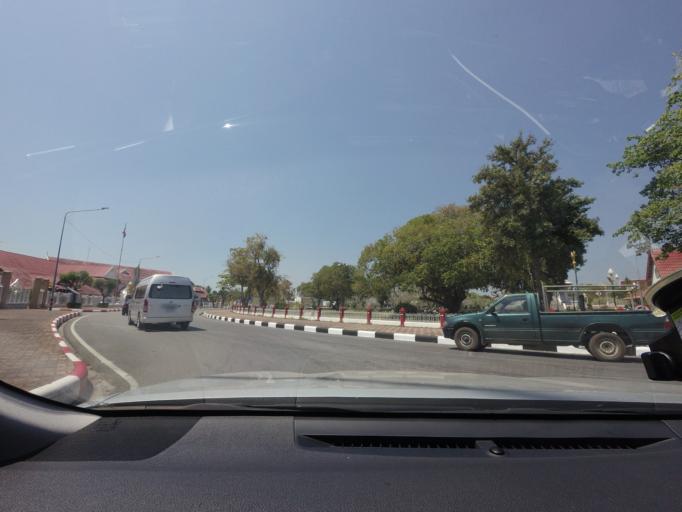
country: TH
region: Yala
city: Yala
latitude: 6.5411
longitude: 101.2813
